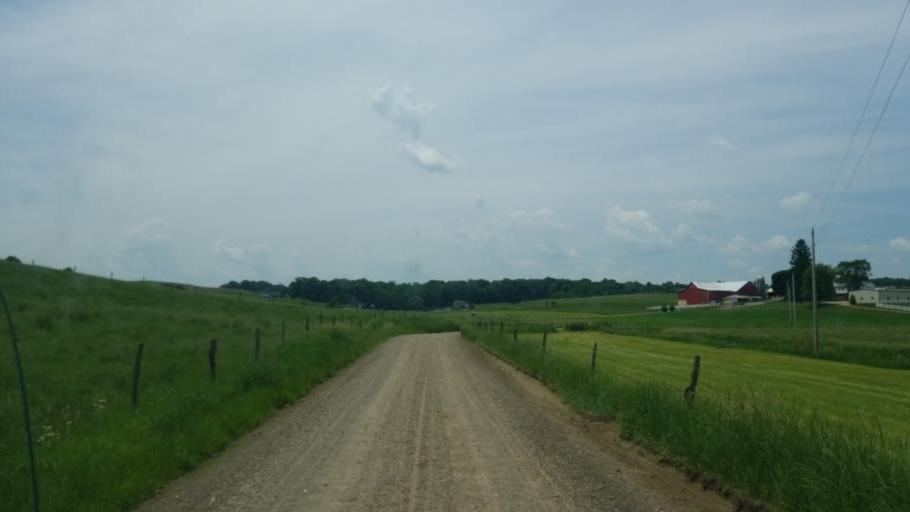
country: US
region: Ohio
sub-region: Tuscarawas County
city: Sugarcreek
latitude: 40.4743
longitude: -81.7644
